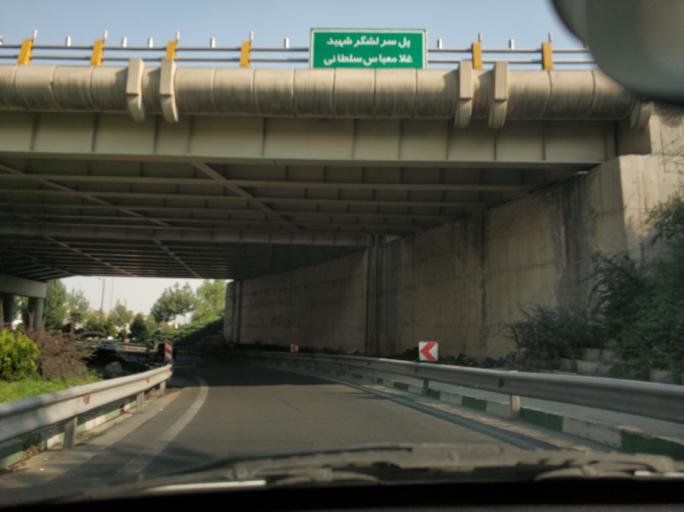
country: IR
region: Tehran
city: Tehran
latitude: 35.7398
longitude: 51.3681
